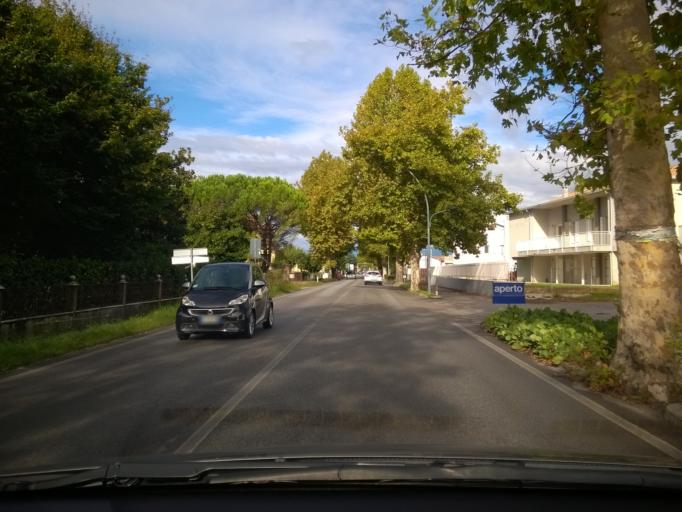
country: IT
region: Veneto
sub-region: Provincia di Treviso
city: Castelfranco Veneto
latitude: 45.6781
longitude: 11.9094
